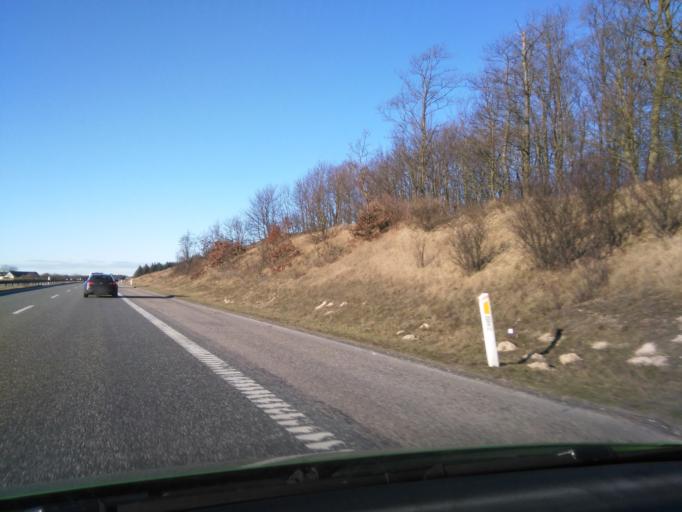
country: DK
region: North Denmark
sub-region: Mariagerfjord Kommune
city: Hobro
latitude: 56.5551
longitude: 9.8724
